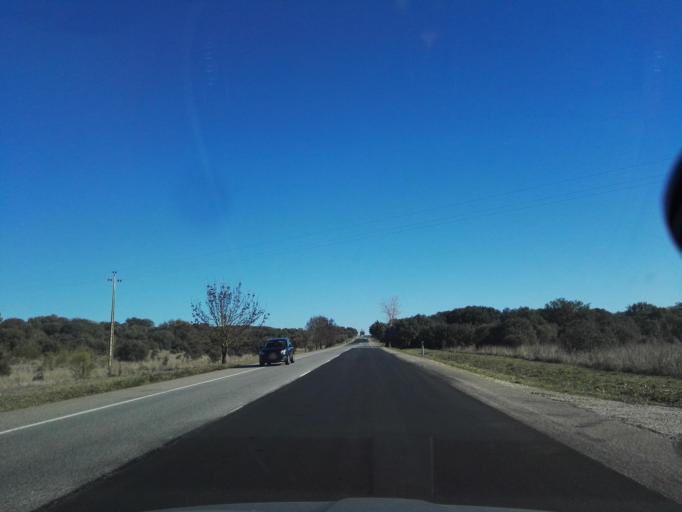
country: PT
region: Evora
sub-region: Estremoz
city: Estremoz
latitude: 38.8331
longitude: -7.5499
